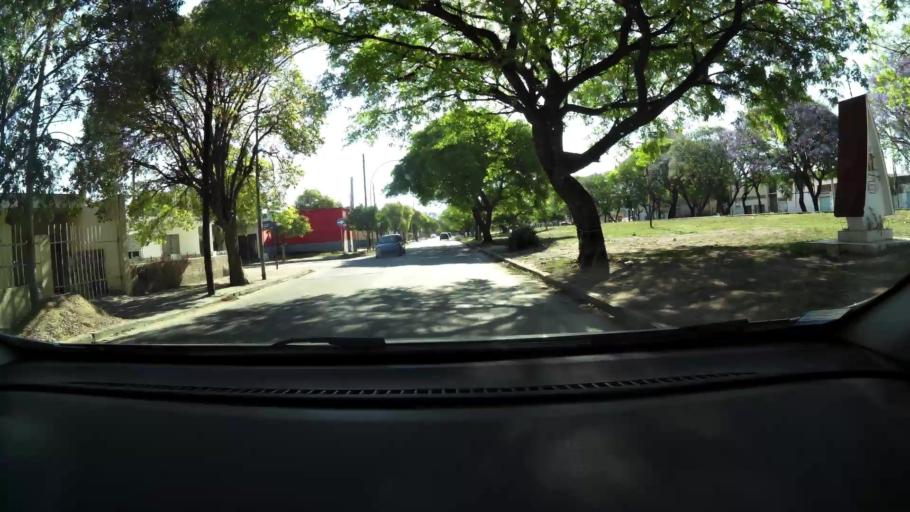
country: AR
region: Cordoba
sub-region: Departamento de Capital
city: Cordoba
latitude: -31.3925
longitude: -64.1476
